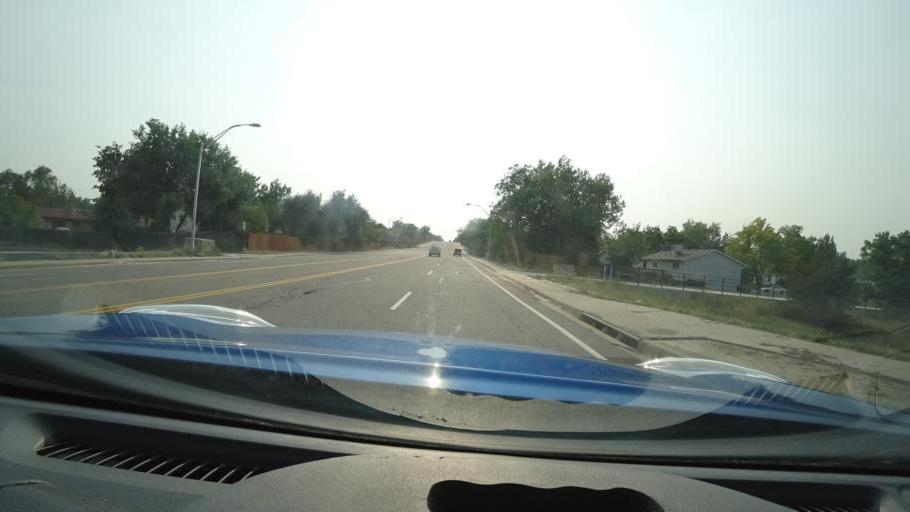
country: US
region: Colorado
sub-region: Adams County
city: Aurora
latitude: 39.6677
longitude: -104.7938
